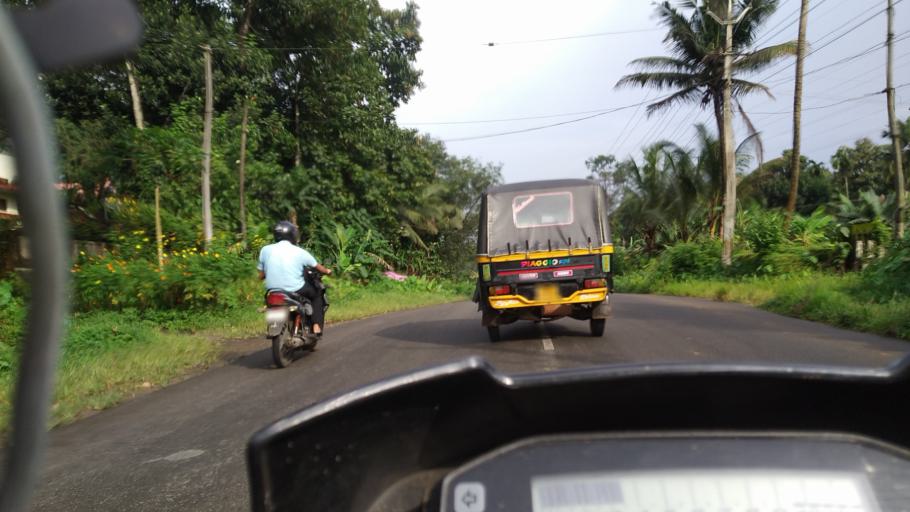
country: IN
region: Kerala
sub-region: Ernakulam
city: Kotamangalam
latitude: 10.0531
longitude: 76.7022
